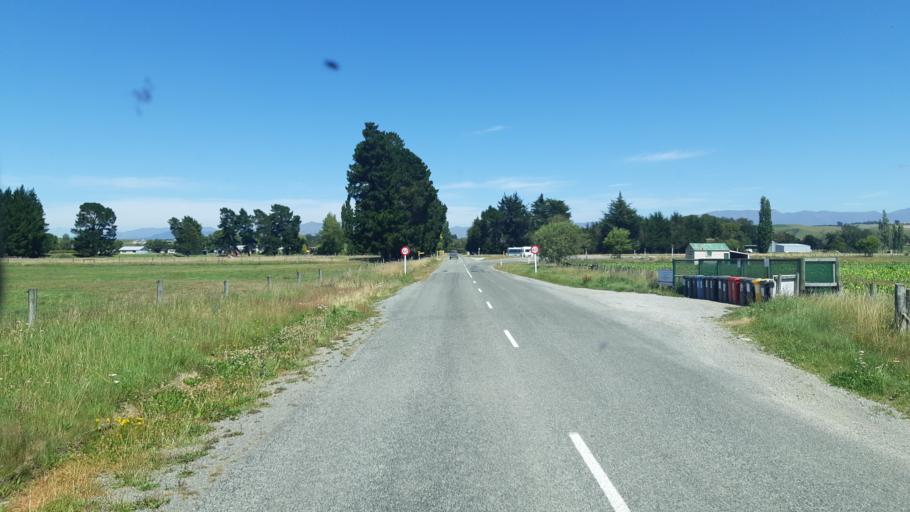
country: NZ
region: Canterbury
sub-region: Timaru District
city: Timaru
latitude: -44.4328
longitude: 171.0858
